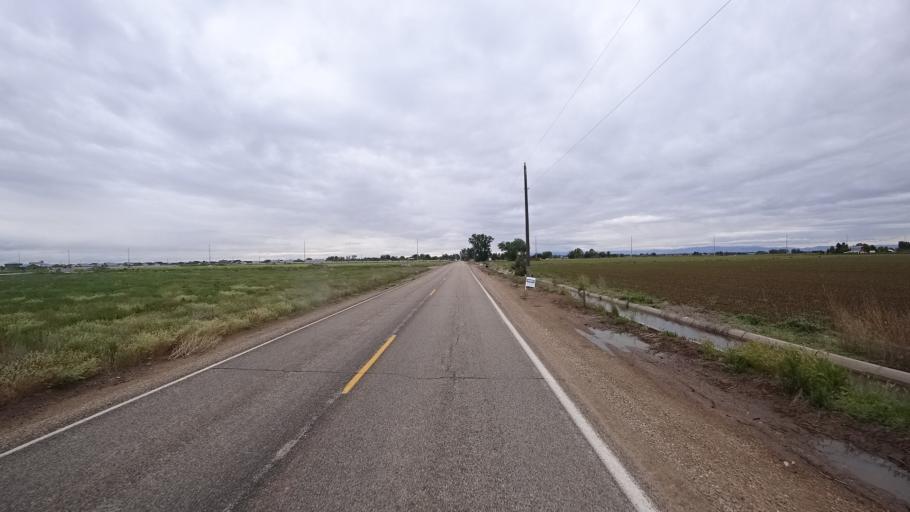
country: US
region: Idaho
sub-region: Ada County
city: Star
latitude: 43.6532
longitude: -116.4735
